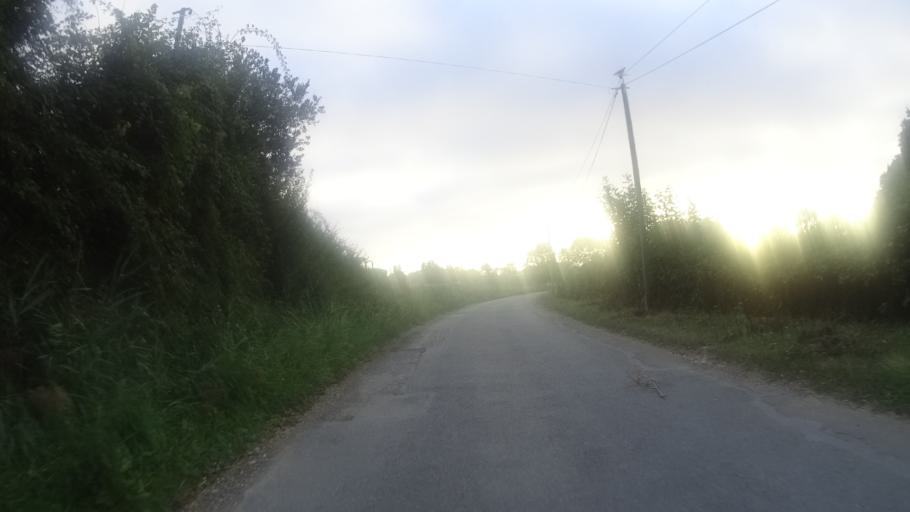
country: FR
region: Ile-de-France
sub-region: Departement de l'Essonne
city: Vert-le-Petit
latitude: 48.5637
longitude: 2.3798
